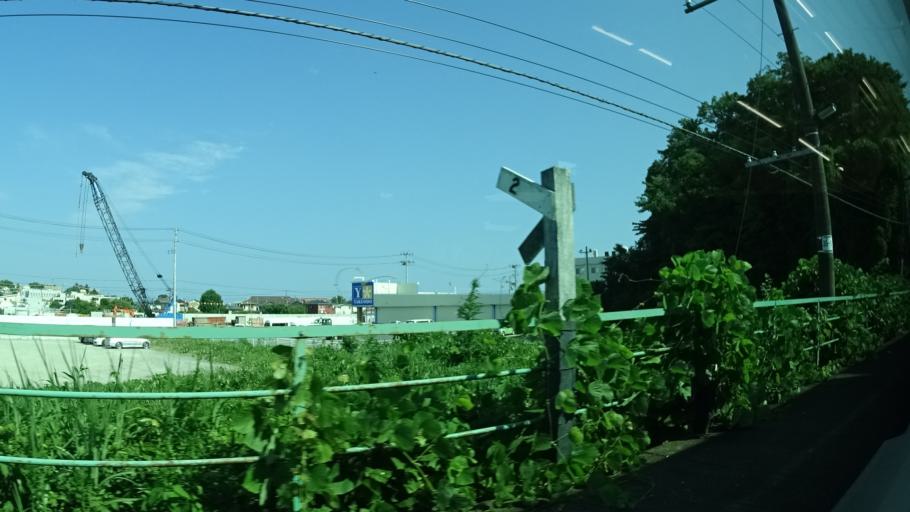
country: JP
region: Miyagi
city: Matsushima
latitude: 38.3815
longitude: 141.0669
